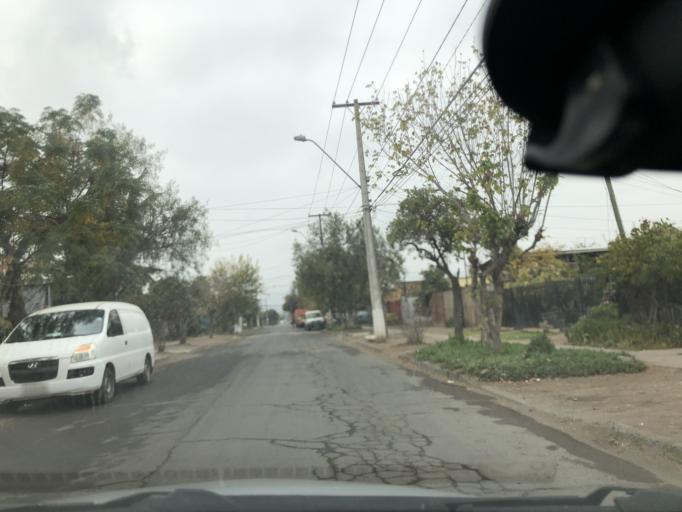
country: CL
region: Santiago Metropolitan
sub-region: Provincia de Santiago
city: La Pintana
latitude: -33.5799
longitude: -70.6050
